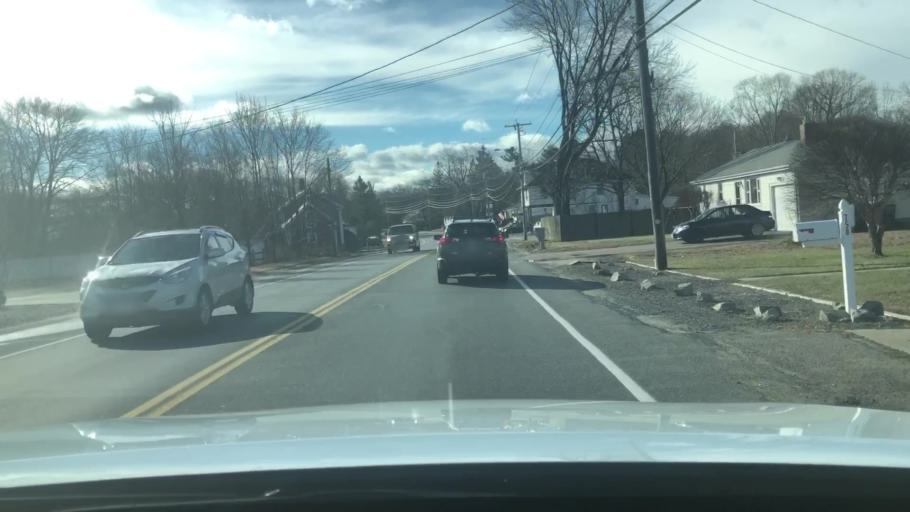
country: US
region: Massachusetts
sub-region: Norfolk County
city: Bellingham
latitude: 42.0480
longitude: -71.4865
